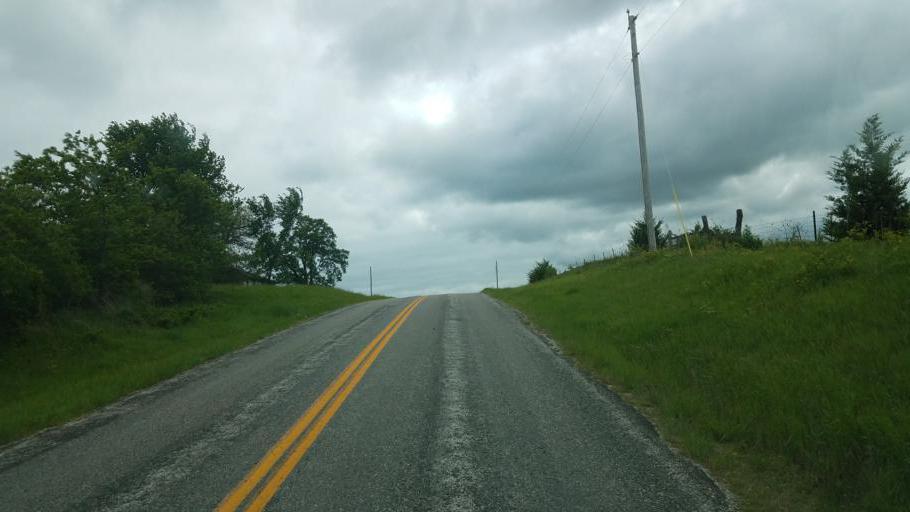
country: US
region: Iowa
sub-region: Decatur County
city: Lamoni
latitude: 40.5593
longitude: -93.8409
